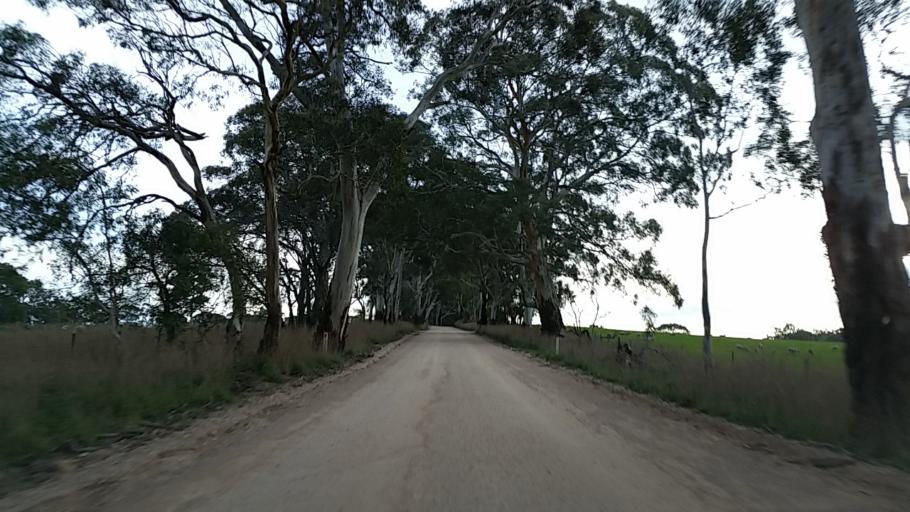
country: AU
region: South Australia
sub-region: Adelaide Hills
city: Birdwood
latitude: -34.8783
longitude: 138.9824
